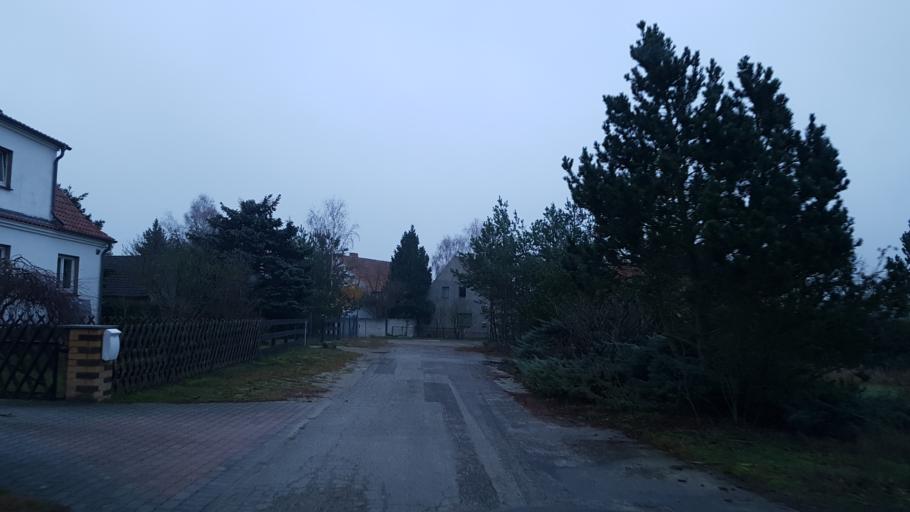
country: DE
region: Brandenburg
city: Ruckersdorf
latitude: 51.5510
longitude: 13.6021
